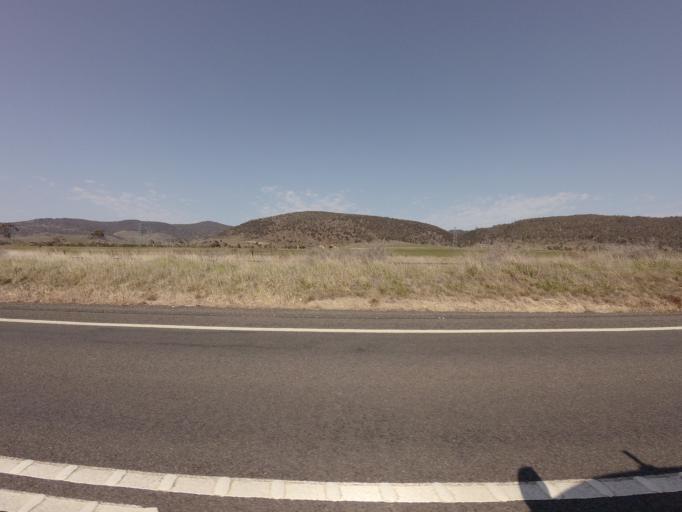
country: AU
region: Tasmania
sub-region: Northern Midlands
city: Evandale
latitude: -41.8123
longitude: 147.6338
